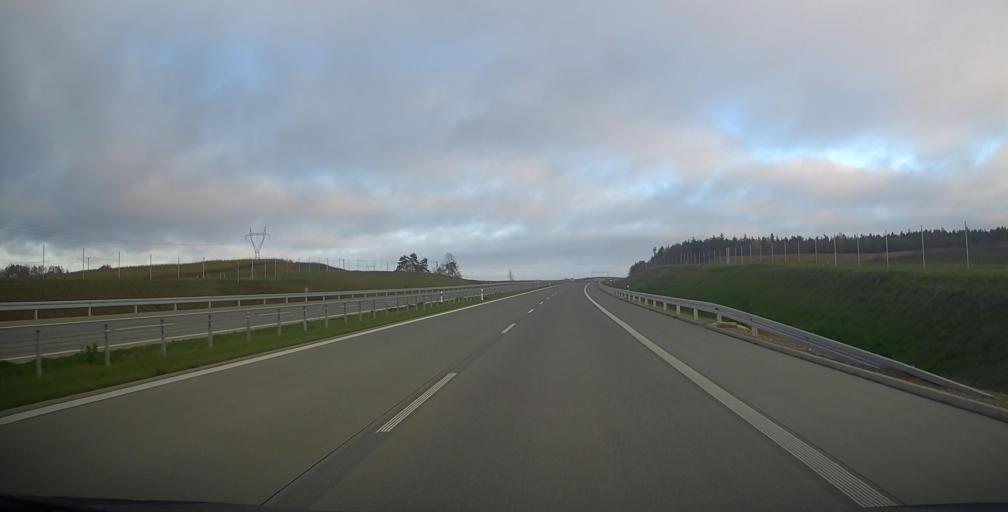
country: PL
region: Podlasie
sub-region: Powiat grajewski
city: Szczuczyn
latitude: 53.6435
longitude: 22.2928
